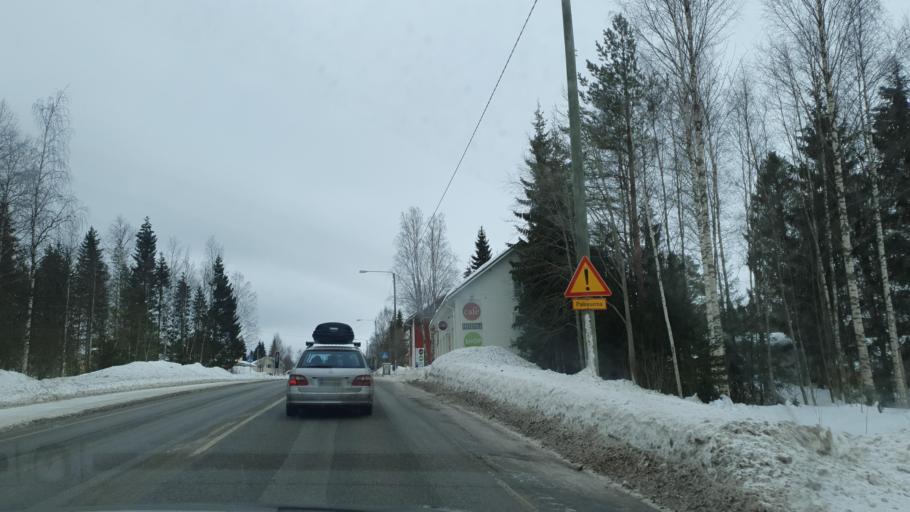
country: FI
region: Lapland
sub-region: Kemi-Tornio
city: Tornio
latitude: 66.0427
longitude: 24.0159
